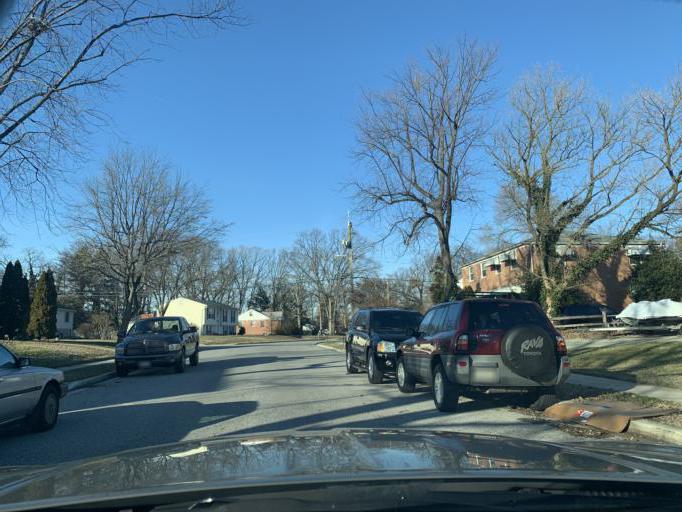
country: US
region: Maryland
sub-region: Anne Arundel County
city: Glen Burnie
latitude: 39.1494
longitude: -76.6254
